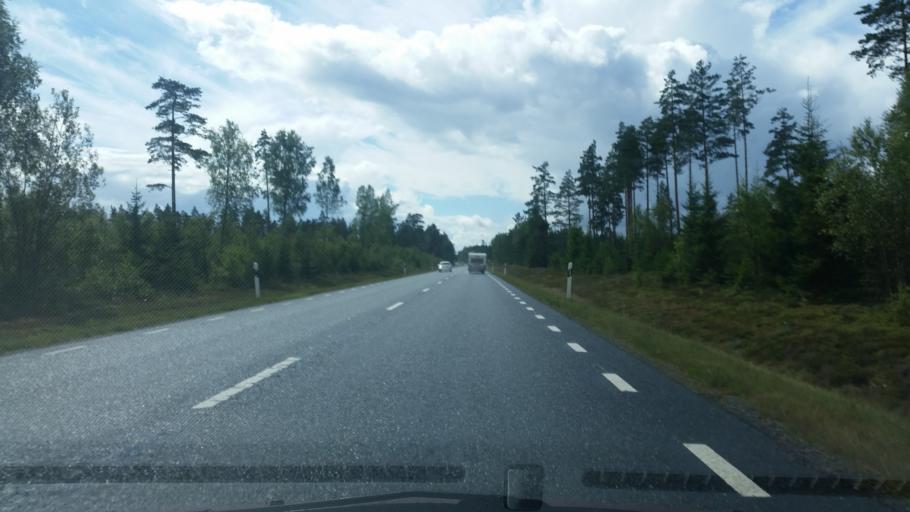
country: SE
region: Joenkoeping
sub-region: Gislaveds Kommun
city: Gislaved
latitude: 57.4002
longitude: 13.5955
